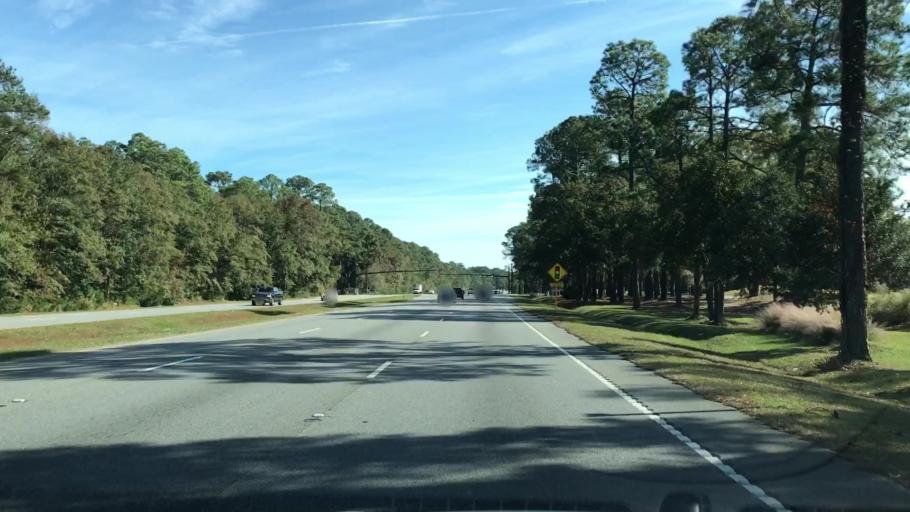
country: US
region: South Carolina
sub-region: Beaufort County
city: Bluffton
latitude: 32.2848
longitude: -80.8847
